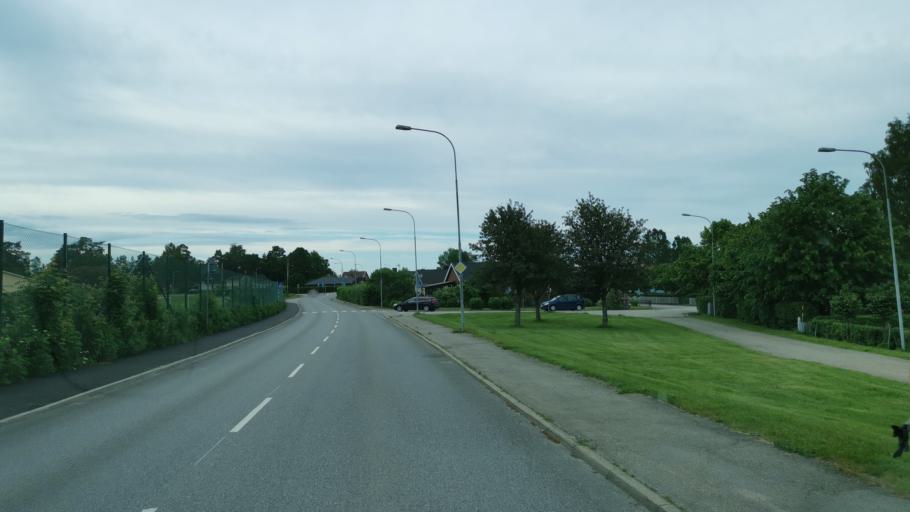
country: SE
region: Vaestra Goetaland
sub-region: Vanersborgs Kommun
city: Vanersborg
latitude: 58.3568
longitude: 12.3523
